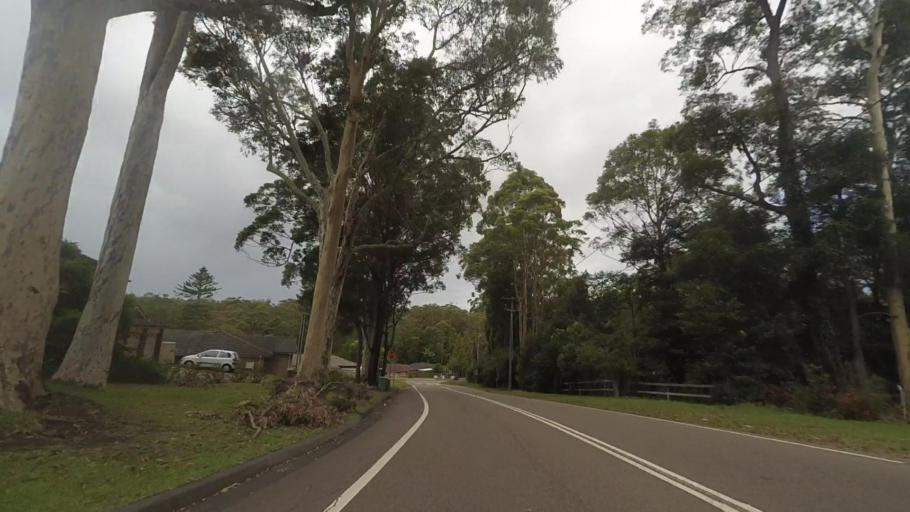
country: AU
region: New South Wales
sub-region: Wyong Shire
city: Berkeley Vale
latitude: -33.3414
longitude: 151.4207
